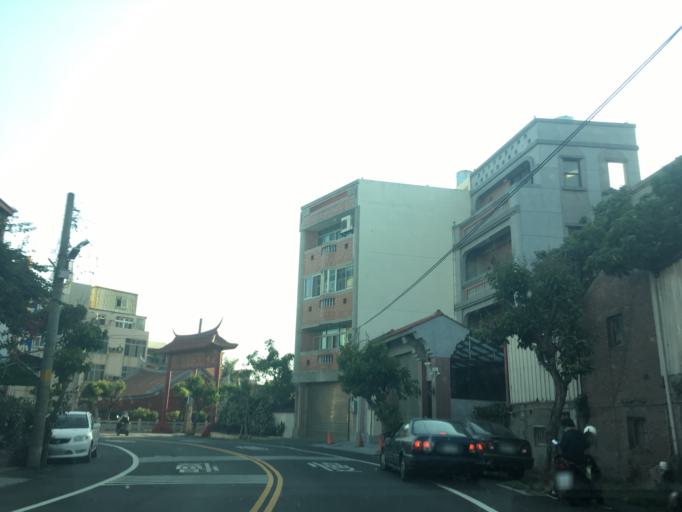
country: TW
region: Taiwan
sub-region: Changhua
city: Chang-hua
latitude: 24.0487
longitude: 120.4373
